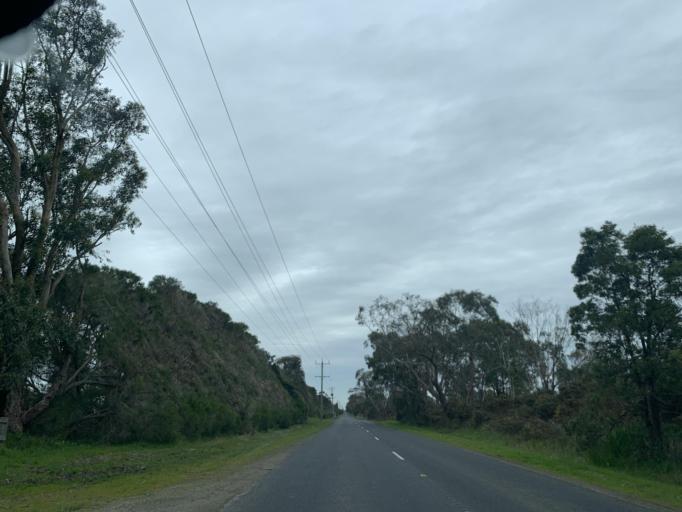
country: AU
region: Victoria
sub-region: Cardinia
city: Garfield
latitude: -38.0838
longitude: 145.6033
